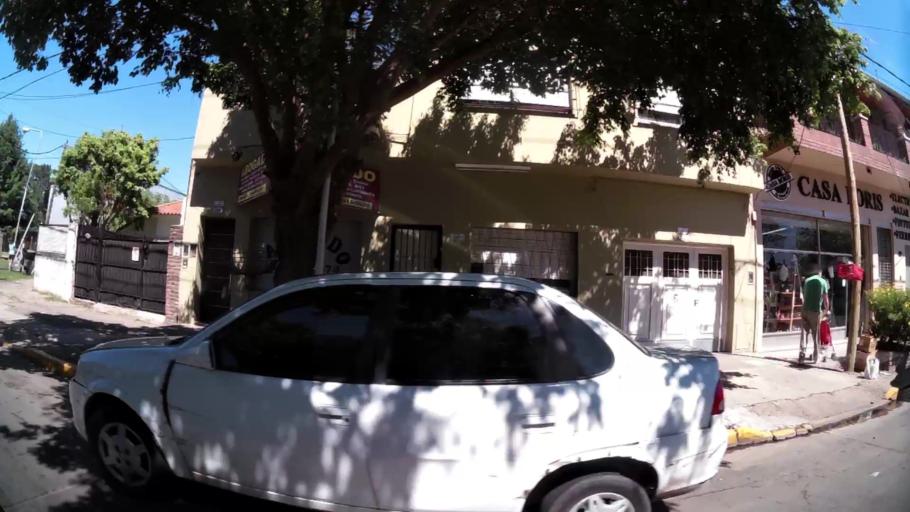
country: AR
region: Buenos Aires
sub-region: Partido de Tigre
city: Tigre
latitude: -34.4981
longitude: -58.6150
